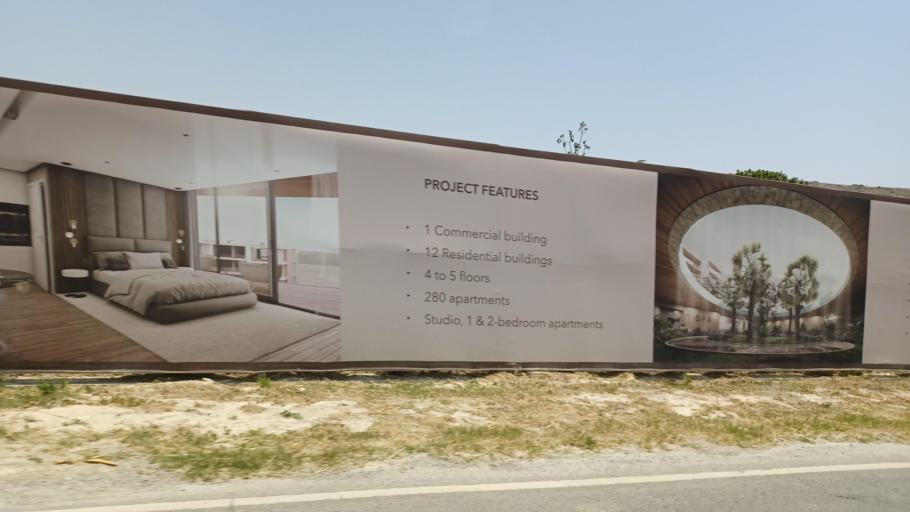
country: CY
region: Larnaka
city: Pyla
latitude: 34.9948
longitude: 33.6943
